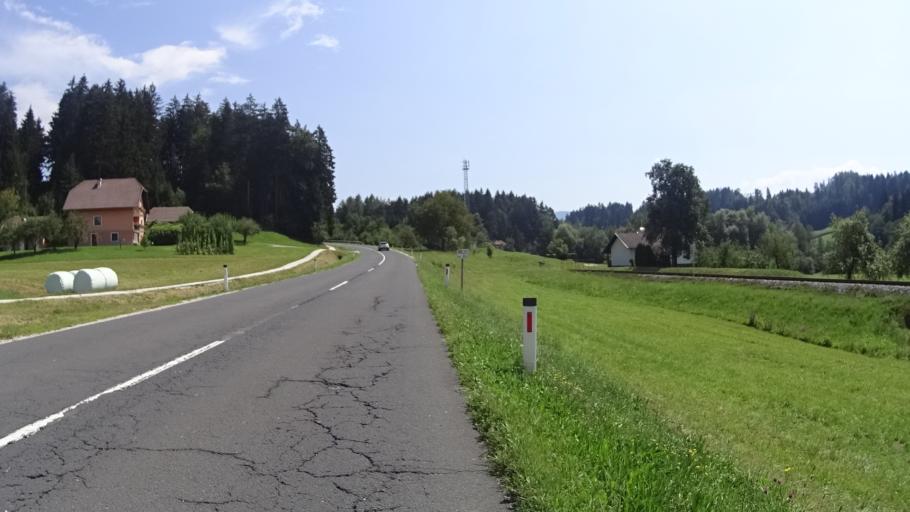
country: SI
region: Mezica
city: Mezica
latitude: 46.5652
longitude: 14.8441
